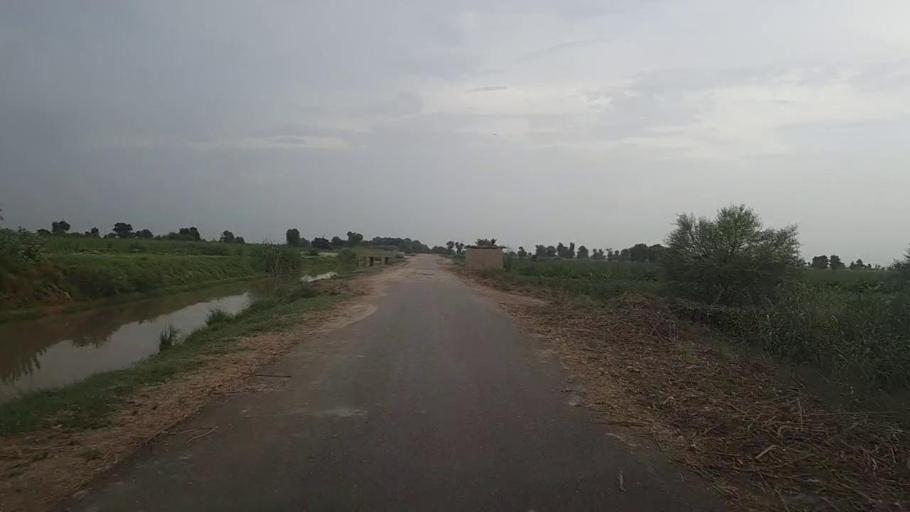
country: PK
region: Sindh
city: Karaundi
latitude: 26.9665
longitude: 68.3639
